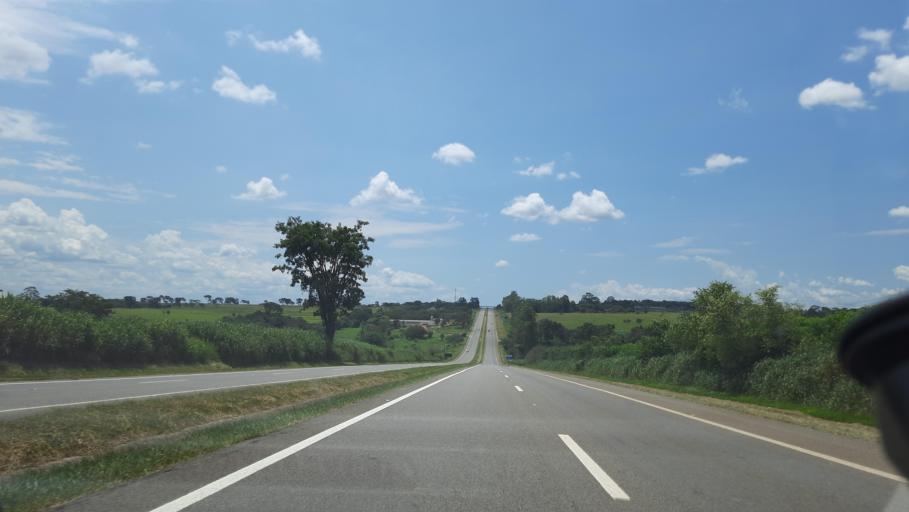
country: BR
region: Sao Paulo
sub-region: Mococa
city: Mococa
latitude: -21.5913
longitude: -47.0395
